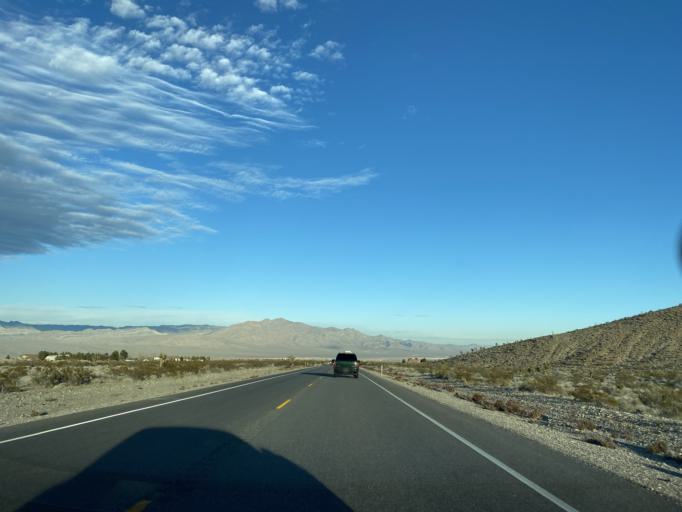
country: US
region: Nevada
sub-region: Clark County
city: Summerlin South
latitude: 36.3069
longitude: -115.4009
